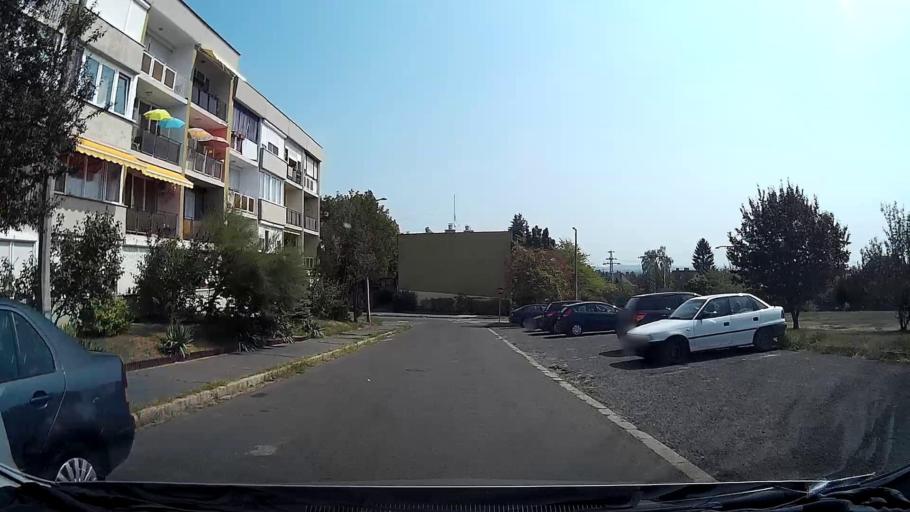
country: HU
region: Pest
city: Szentendre
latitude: 47.6667
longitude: 19.0607
